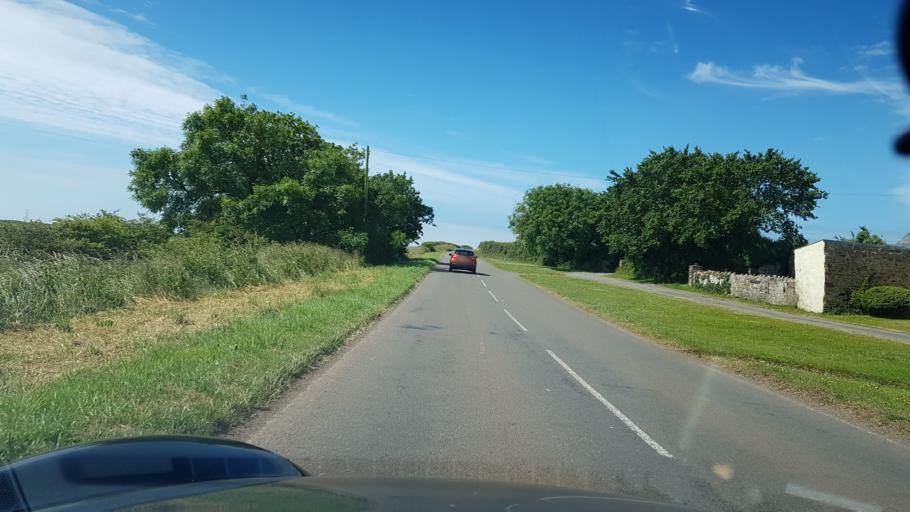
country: GB
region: Wales
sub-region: Pembrokeshire
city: Dale
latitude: 51.7489
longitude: -5.1415
